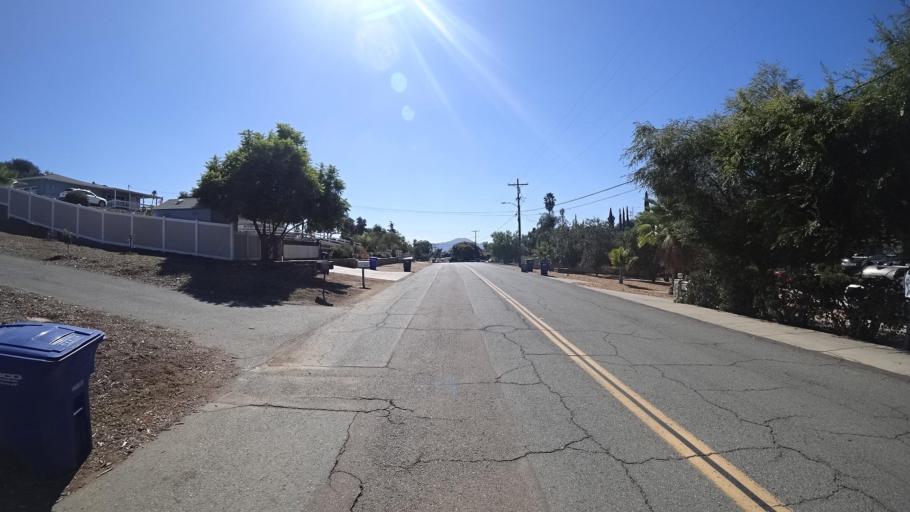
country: US
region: California
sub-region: San Diego County
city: Bostonia
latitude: 32.8176
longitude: -116.9303
